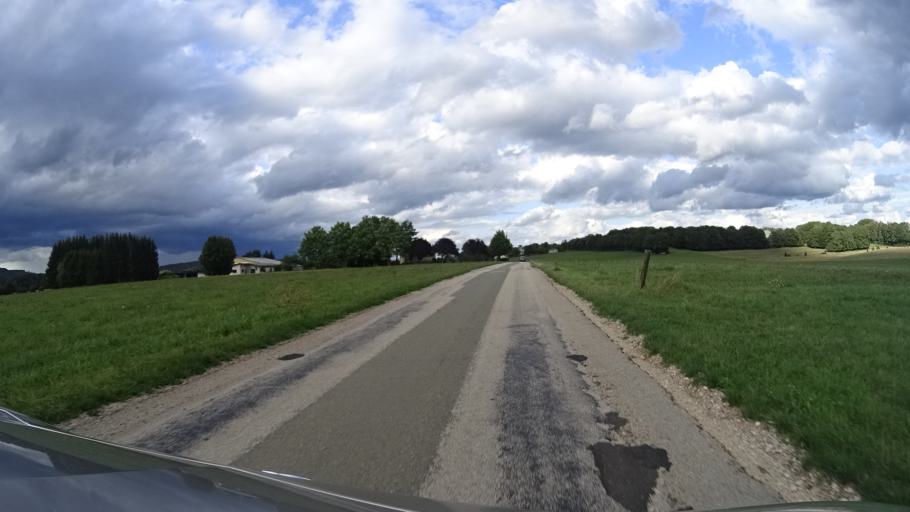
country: FR
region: Franche-Comte
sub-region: Departement du Doubs
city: Nancray
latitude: 47.2374
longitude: 6.1705
